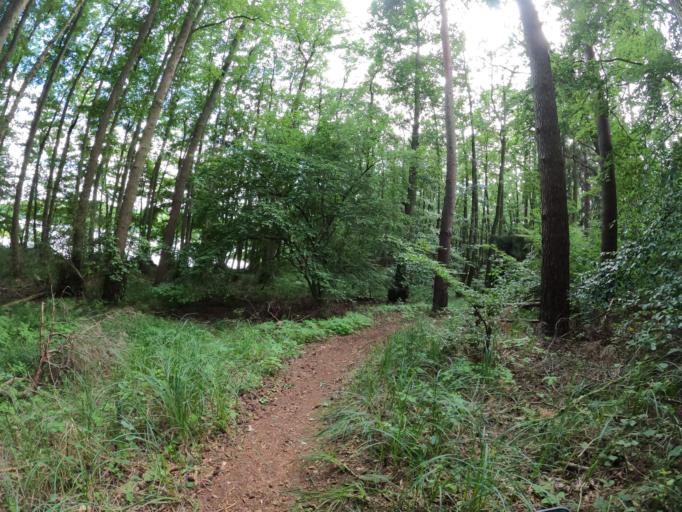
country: DE
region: Brandenburg
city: Angermunde
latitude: 53.0288
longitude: 13.9333
